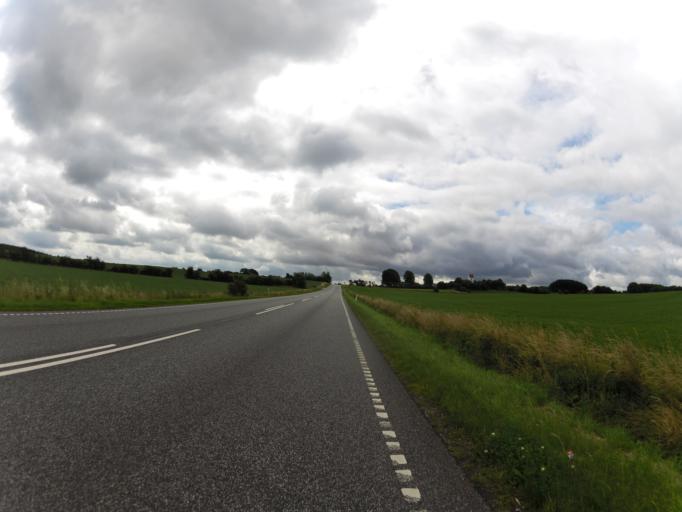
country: DK
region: North Denmark
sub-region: Mariagerfjord Kommune
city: Hadsund
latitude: 56.6772
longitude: 10.1444
